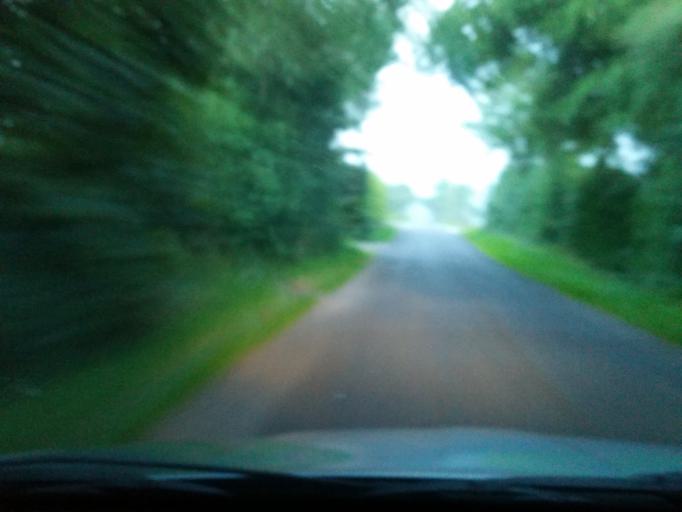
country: IE
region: Ulster
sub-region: County Monaghan
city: Clones
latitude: 54.2610
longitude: -7.2721
